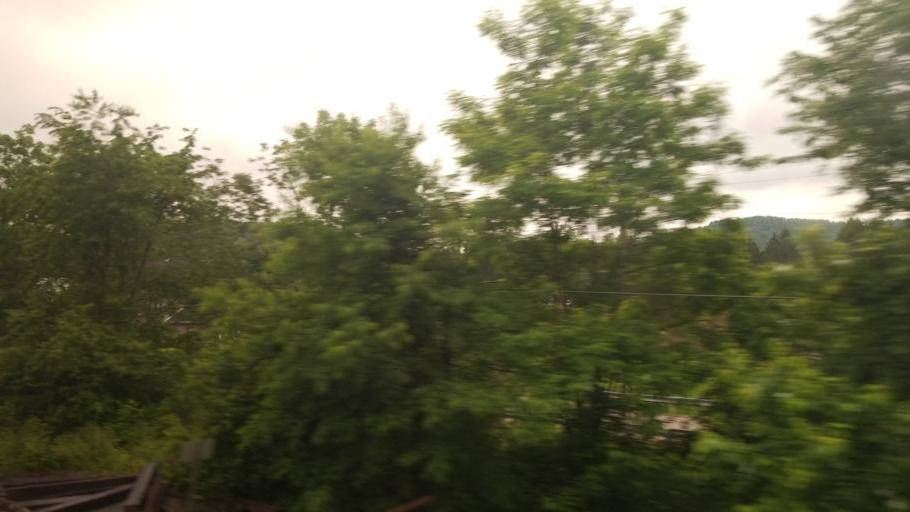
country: US
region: Pennsylvania
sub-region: Fayette County
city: South Connellsville
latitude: 39.8144
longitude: -79.3615
